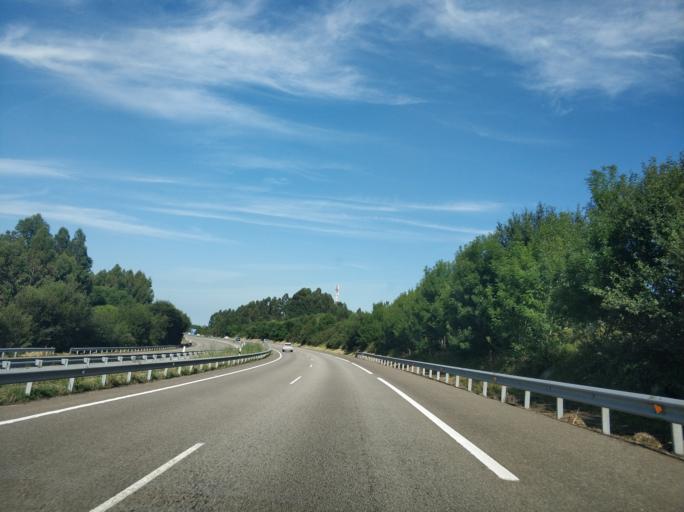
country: ES
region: Asturias
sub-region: Province of Asturias
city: Castrillon
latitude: 43.5428
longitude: -6.0239
